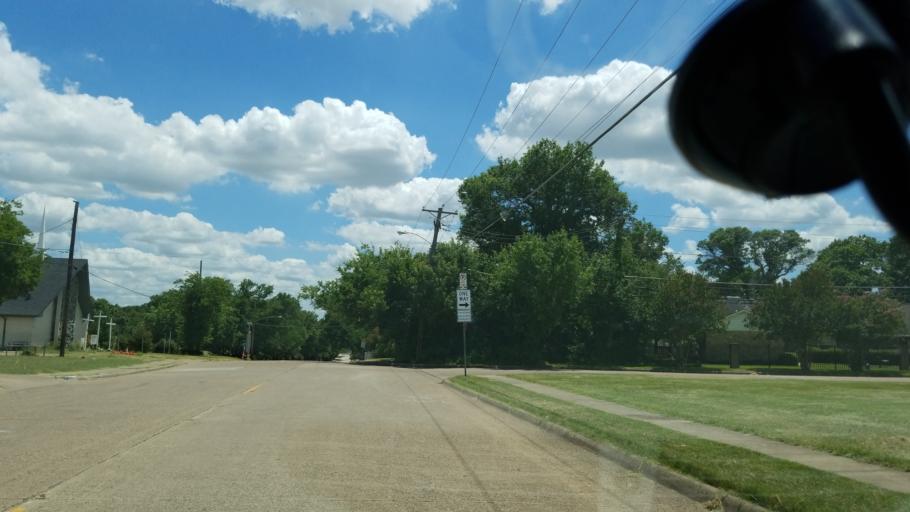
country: US
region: Texas
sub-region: Dallas County
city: Cockrell Hill
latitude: 32.6957
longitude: -96.8743
